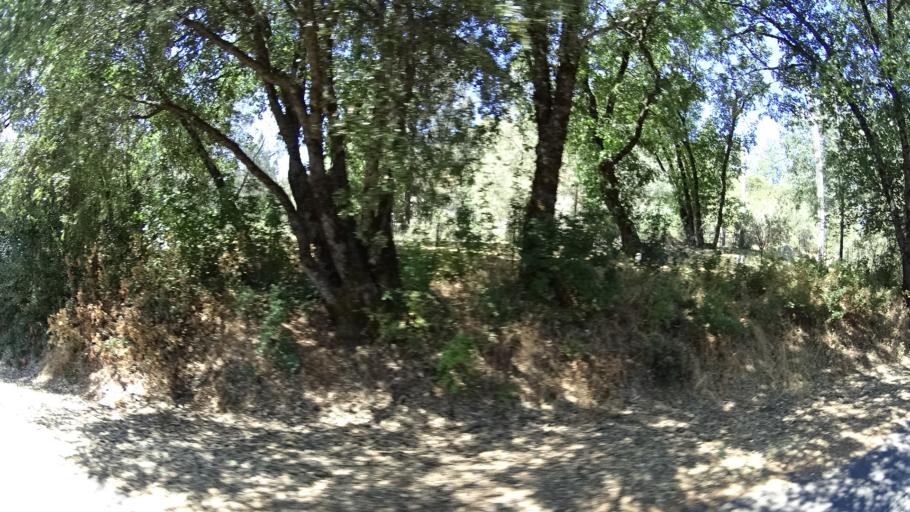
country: US
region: California
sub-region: Calaveras County
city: Forest Meadows
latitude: 38.1770
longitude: -120.3809
